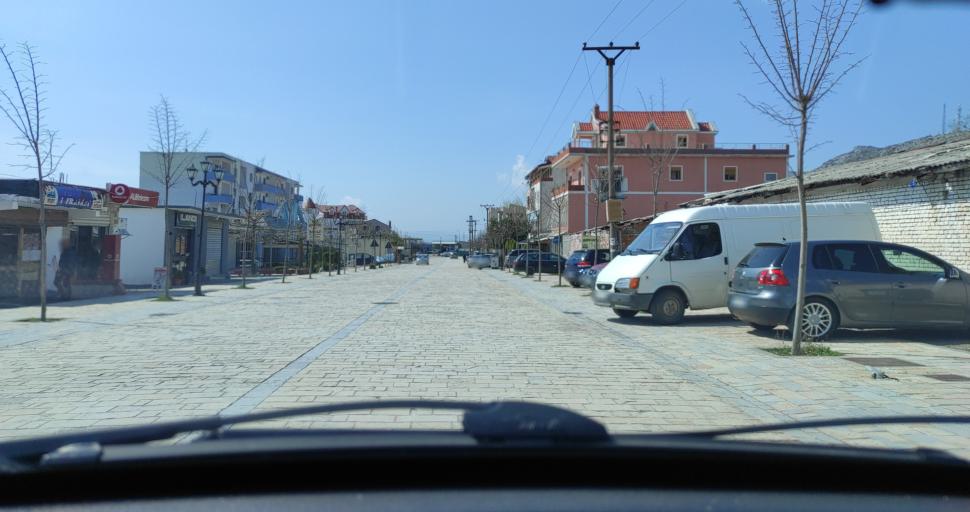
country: AL
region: Shkoder
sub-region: Rrethi i Shkodres
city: Vau i Dejes
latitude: 42.0076
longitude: 19.6392
